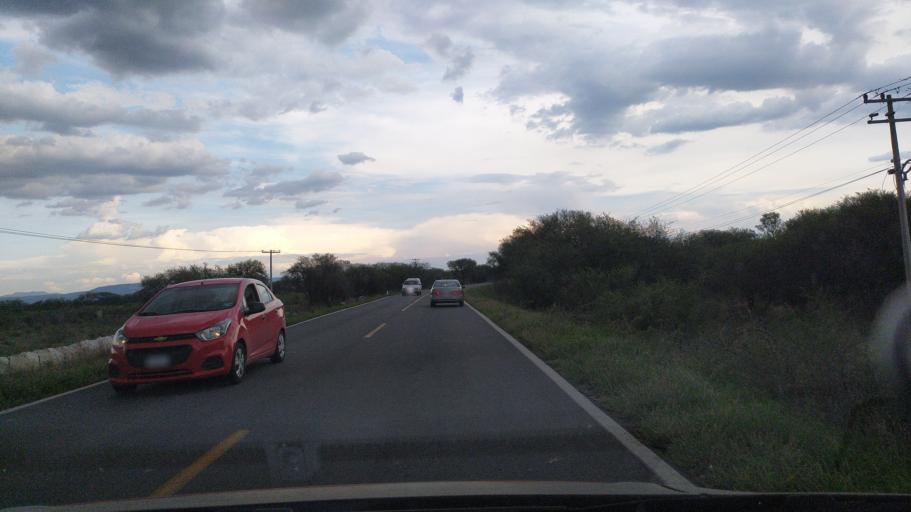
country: MX
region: Guanajuato
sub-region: San Francisco del Rincon
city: San Ignacio de Hidalgo
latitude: 20.8214
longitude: -101.9026
